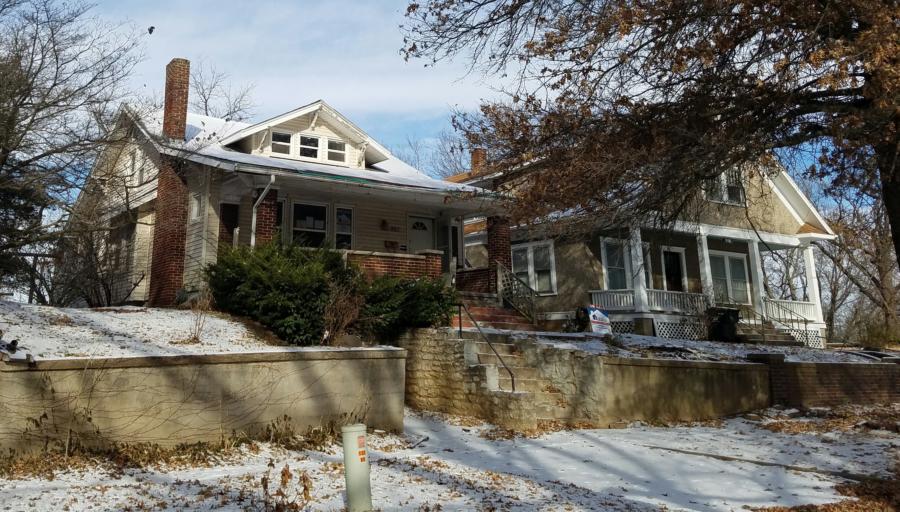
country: US
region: Missouri
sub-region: Lafayette County
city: Lexington
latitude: 39.1867
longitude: -93.8853
